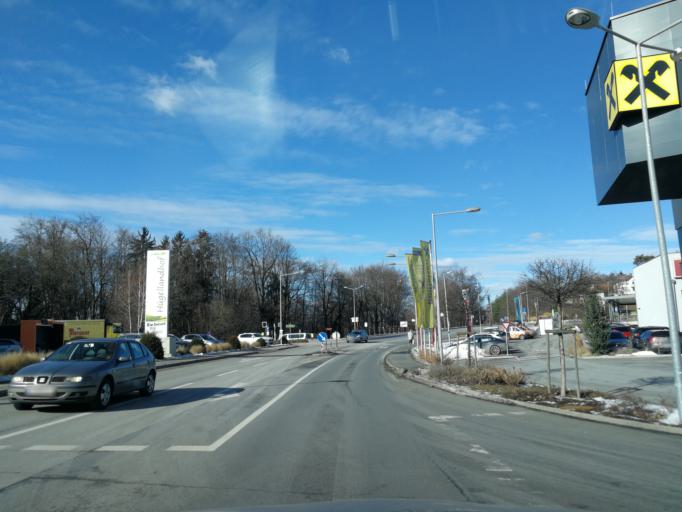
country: AT
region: Styria
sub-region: Politischer Bezirk Graz-Umgebung
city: Nestelbach bei Graz
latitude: 47.0576
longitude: 15.5998
